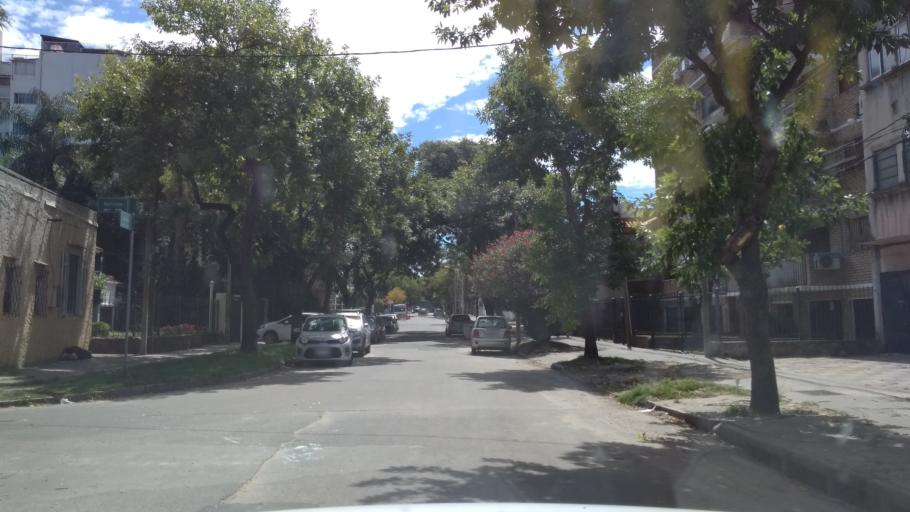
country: UY
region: Montevideo
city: Montevideo
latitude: -34.8960
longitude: -56.1183
